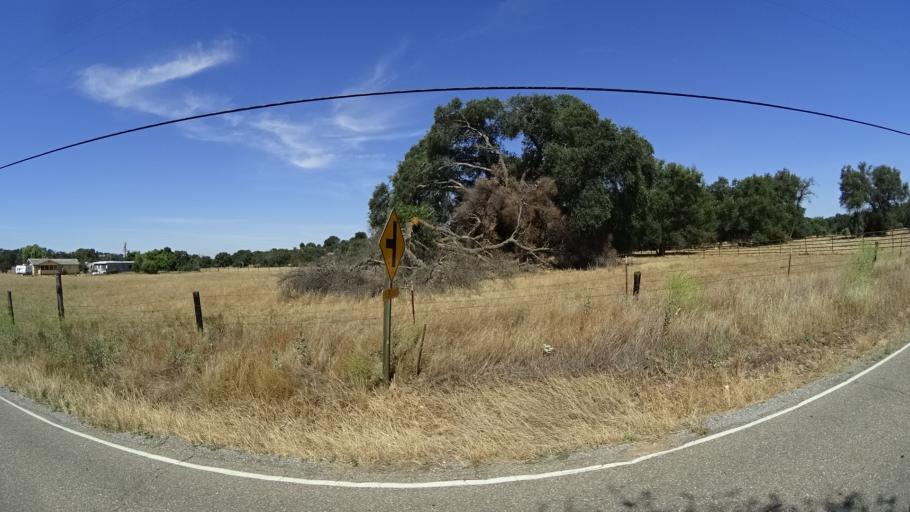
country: US
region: California
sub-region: Calaveras County
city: Rancho Calaveras
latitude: 38.1424
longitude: -120.8992
